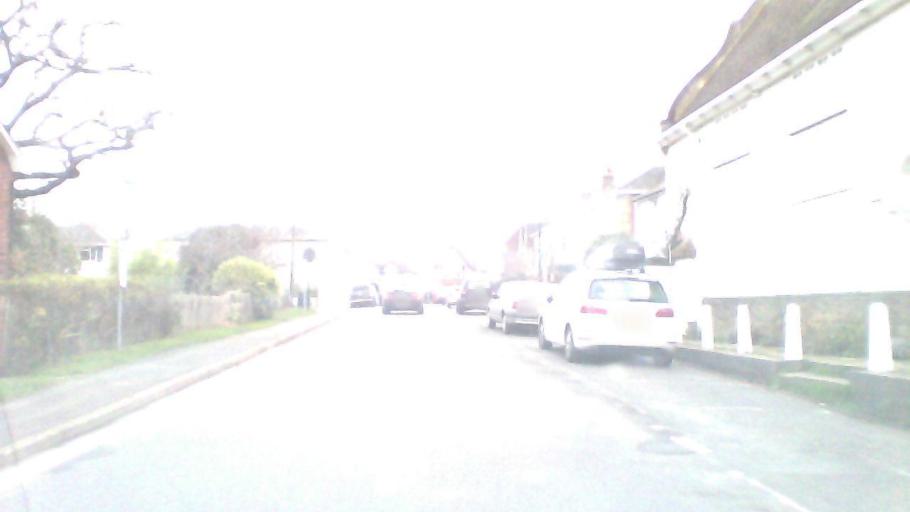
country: GB
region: England
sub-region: Isle of Wight
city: Bembridge
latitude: 50.6914
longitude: -1.0897
